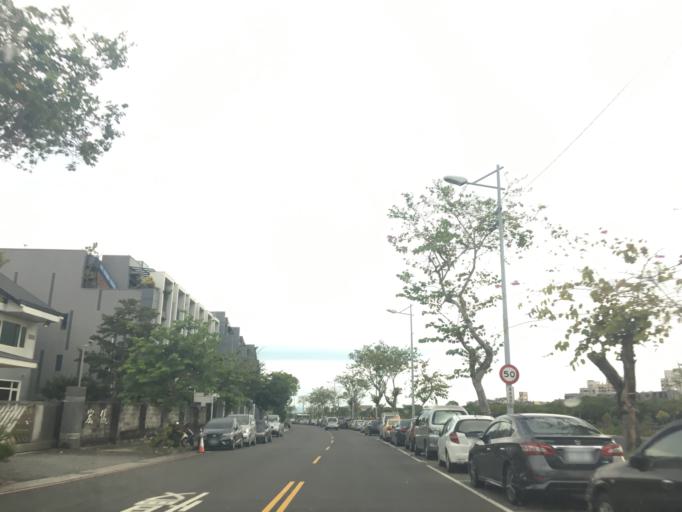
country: TW
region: Taiwan
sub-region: Taichung City
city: Taichung
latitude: 24.1528
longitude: 120.7260
